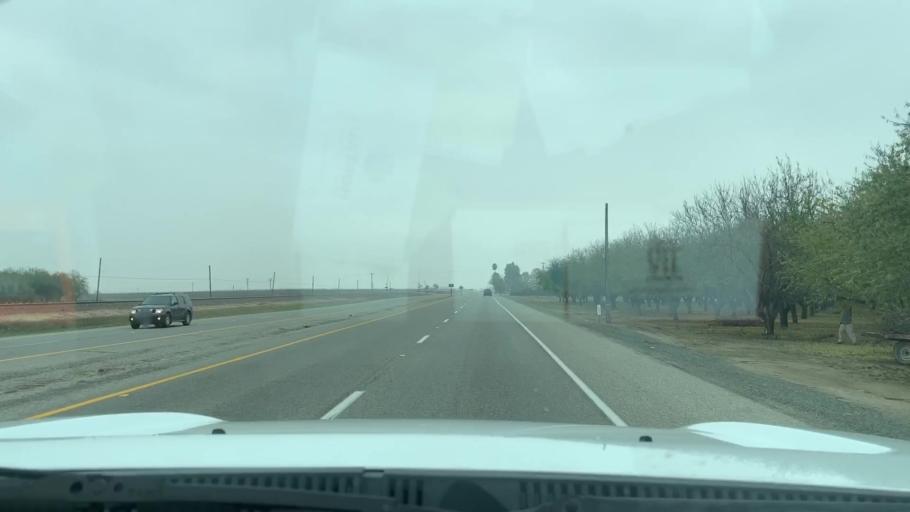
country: US
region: California
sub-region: Kern County
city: Shafter
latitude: 35.5312
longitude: -119.3089
